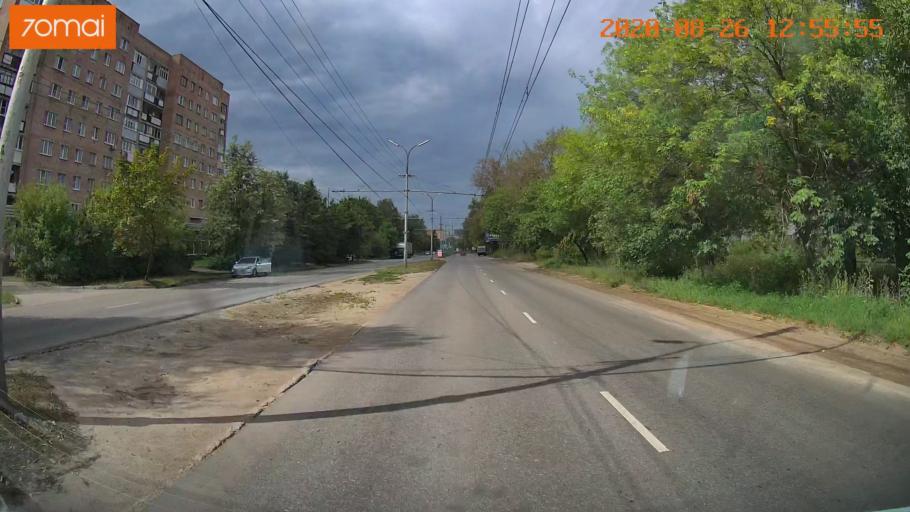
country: RU
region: Rjazan
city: Ryazan'
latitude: 54.6109
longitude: 39.7561
